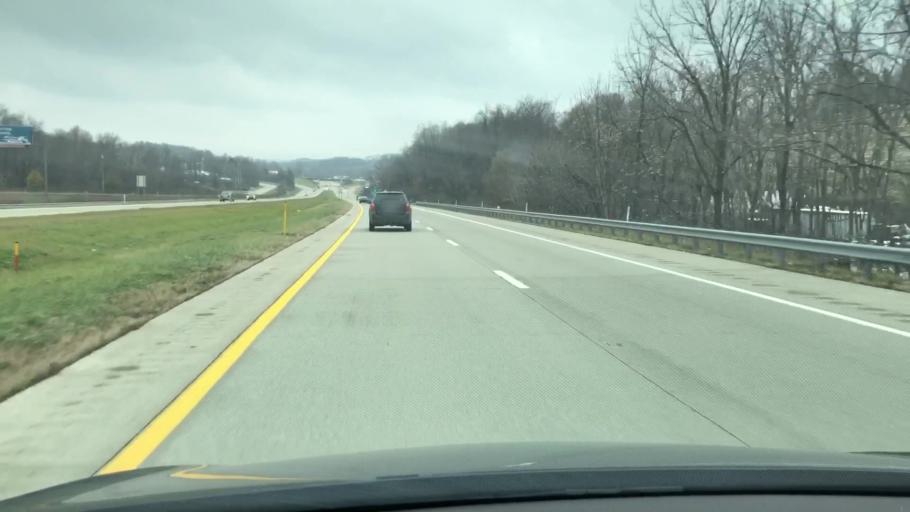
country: US
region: Pennsylvania
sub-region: Westmoreland County
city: Mount Pleasant
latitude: 40.1633
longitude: -79.5610
